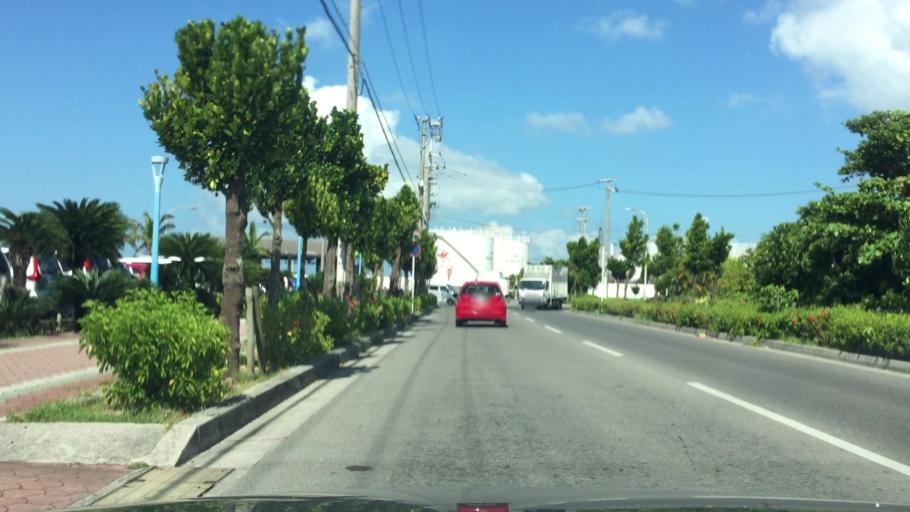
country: JP
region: Okinawa
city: Ishigaki
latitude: 24.3379
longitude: 124.1553
